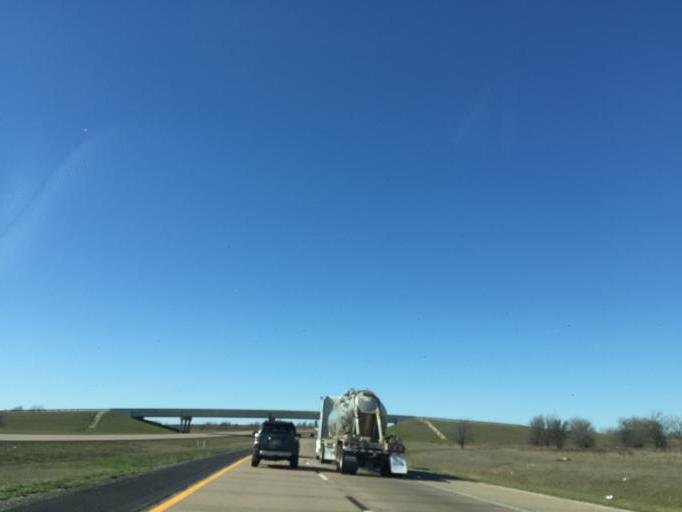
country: US
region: Texas
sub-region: Parker County
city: Aledo
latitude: 32.6963
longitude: -97.5349
